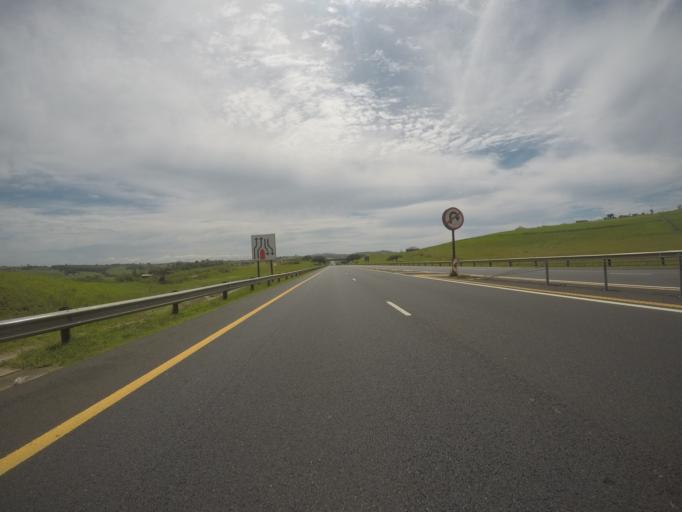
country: ZA
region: KwaZulu-Natal
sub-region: iLembe District Municipality
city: Mandeni
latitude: -29.1747
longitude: 31.5112
